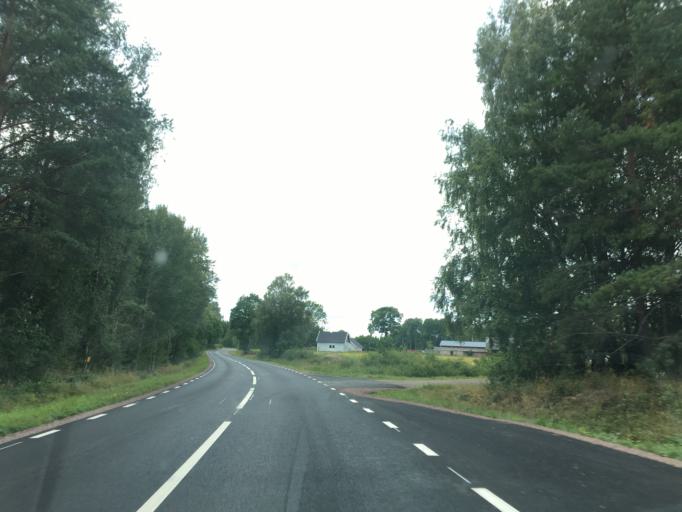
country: SE
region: Kalmar
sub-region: Nybro Kommun
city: Nybro
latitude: 56.9184
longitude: 15.9866
